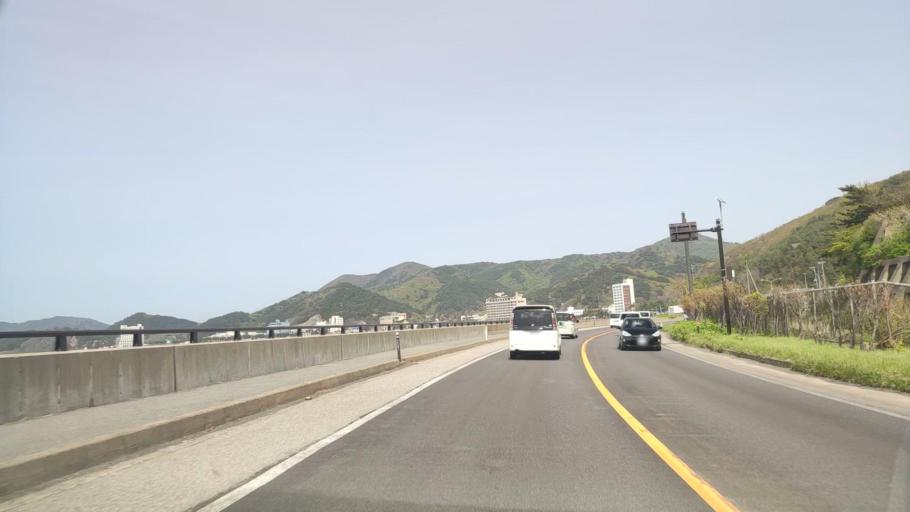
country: JP
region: Aomori
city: Aomori Shi
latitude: 40.8848
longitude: 140.8522
